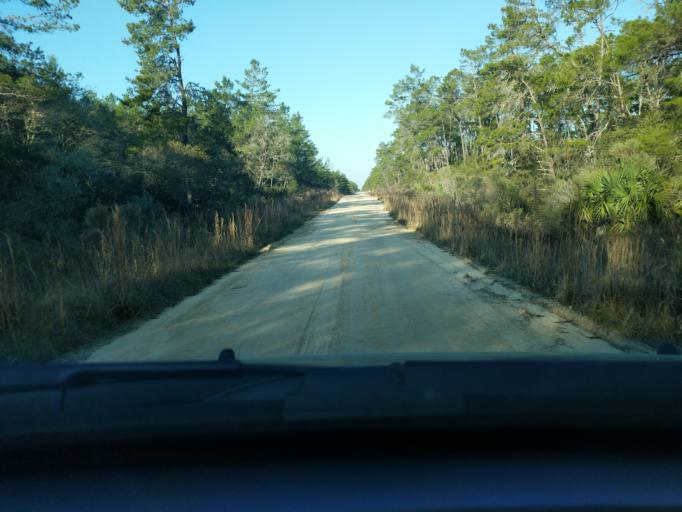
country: US
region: Florida
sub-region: Lake County
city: Astor
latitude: 29.2260
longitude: -81.7663
